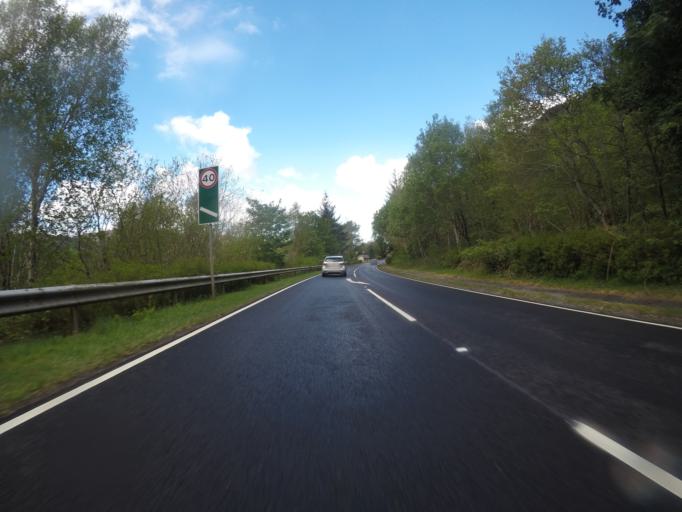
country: GB
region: Scotland
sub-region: Highland
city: Fort William
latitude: 57.2400
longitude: -5.4537
